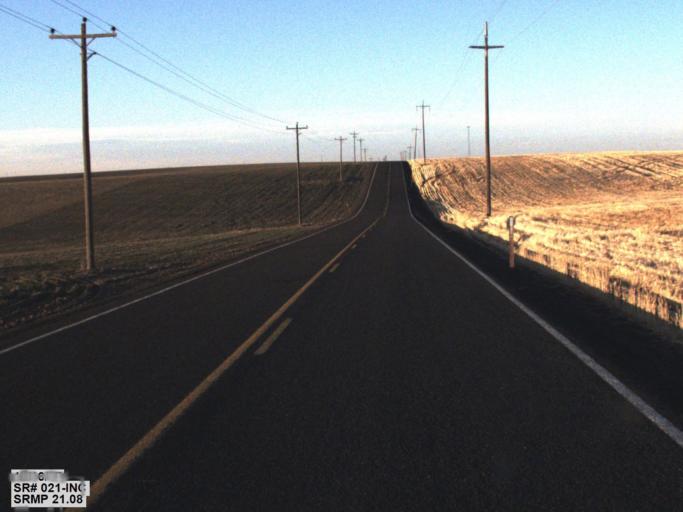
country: US
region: Washington
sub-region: Adams County
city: Ritzville
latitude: 46.9255
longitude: -118.5671
